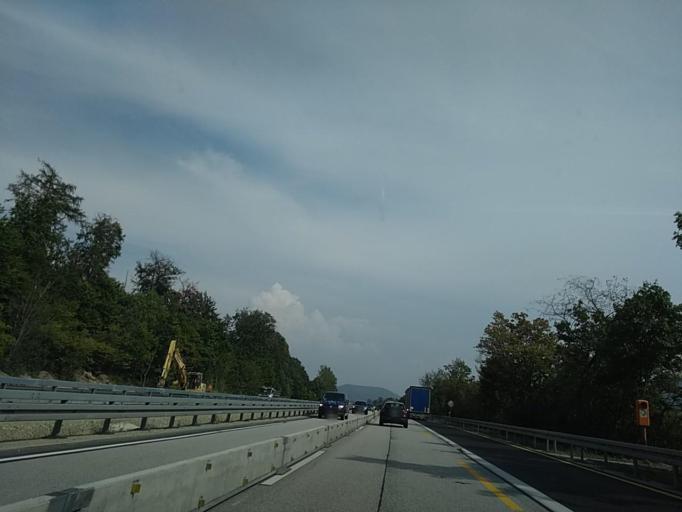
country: DE
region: Hesse
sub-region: Regierungsbezirk Kassel
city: Breuna
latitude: 51.3819
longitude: 9.2375
